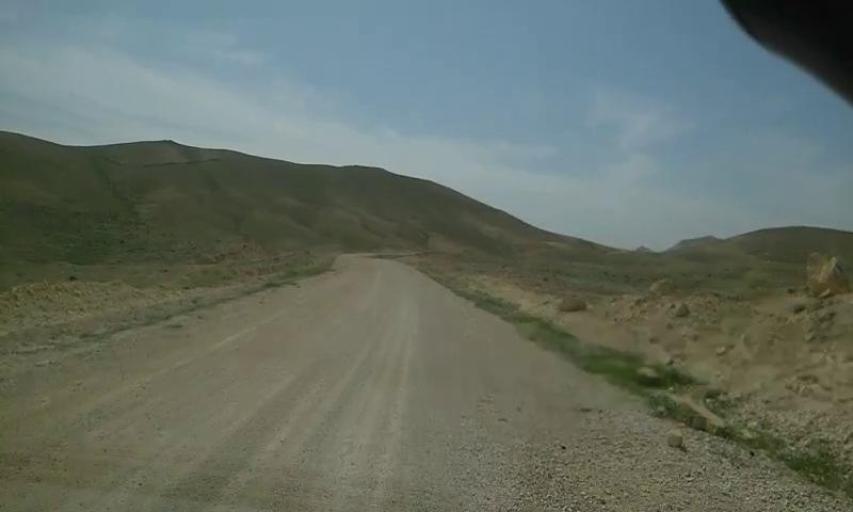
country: PS
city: `Arab ar Rashaydah
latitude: 31.4843
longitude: 35.2801
